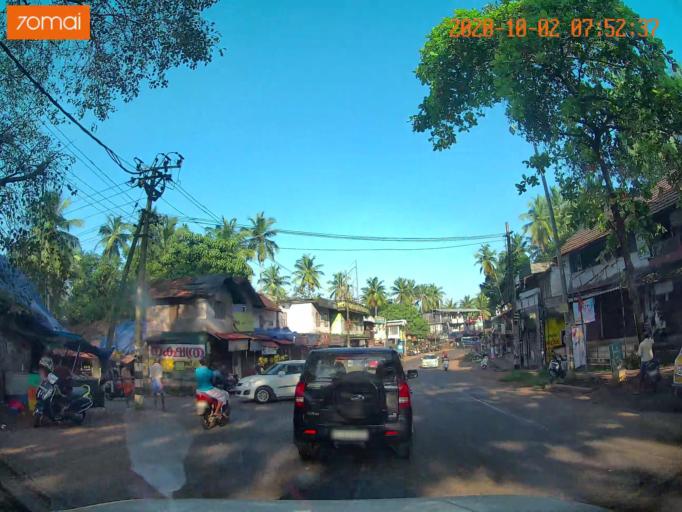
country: IN
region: Kerala
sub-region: Kozhikode
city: Ferokh
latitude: 11.1632
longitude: 75.8783
